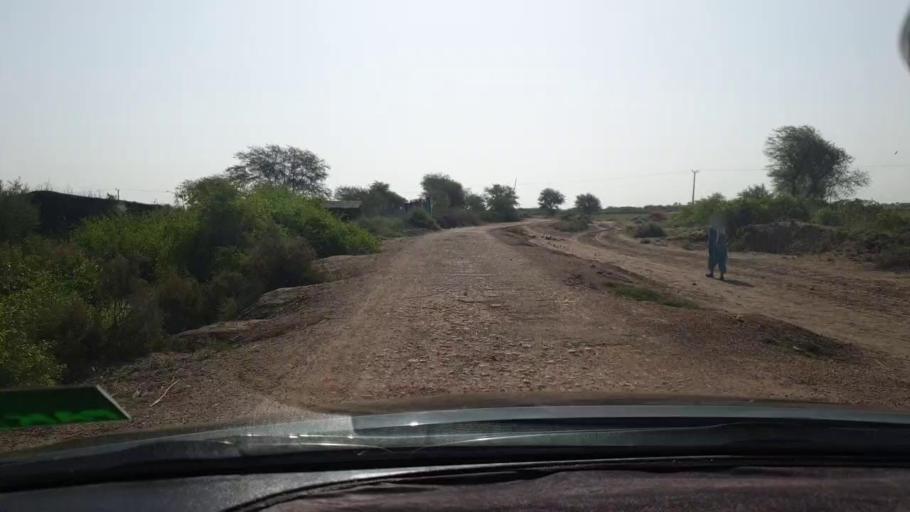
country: PK
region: Sindh
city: Tando Bago
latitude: 24.7123
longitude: 68.9862
